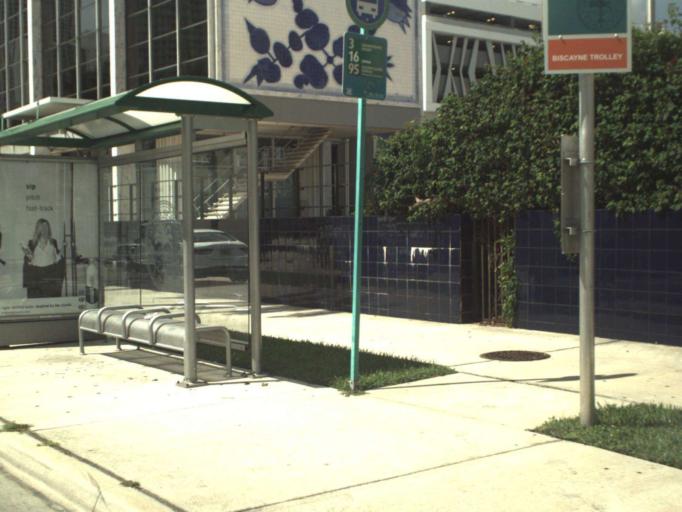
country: US
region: Florida
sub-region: Miami-Dade County
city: Miami
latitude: 25.7978
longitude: -80.1891
